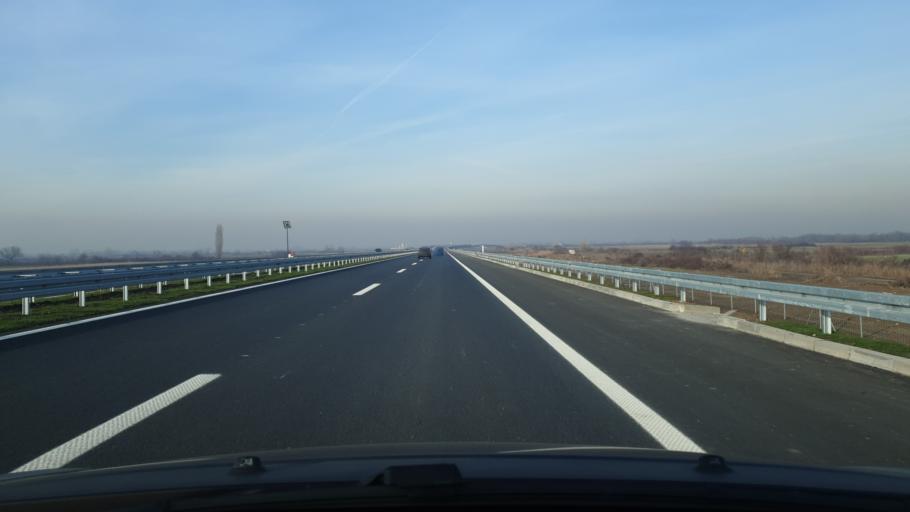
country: RS
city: Boljevci
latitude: 44.7066
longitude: 20.2618
